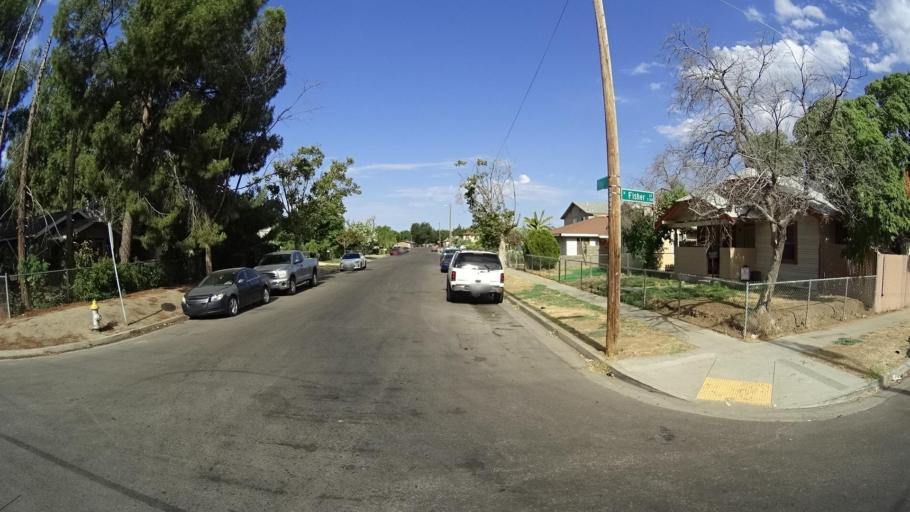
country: US
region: California
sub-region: Fresno County
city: Fresno
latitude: 36.7568
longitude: -119.7703
